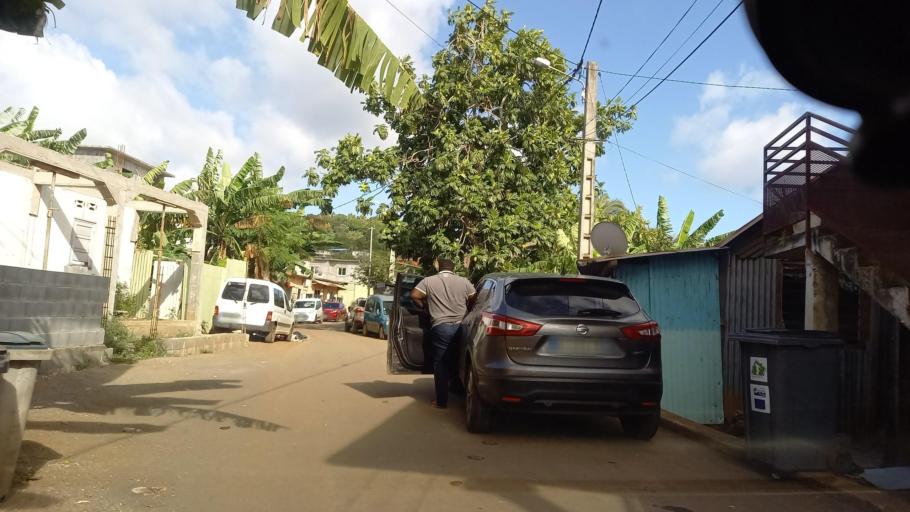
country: YT
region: Bandrele
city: Bandrele
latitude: -12.9105
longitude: 45.1944
